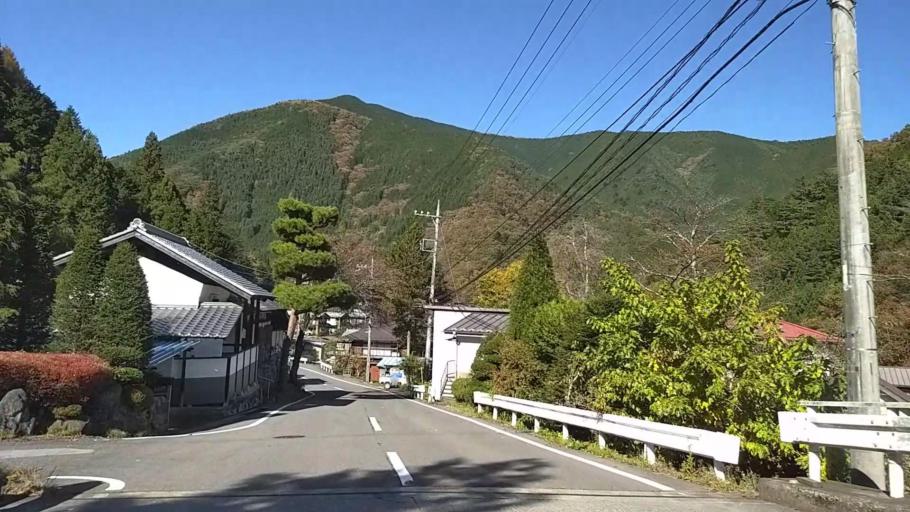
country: JP
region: Yamanashi
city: Otsuki
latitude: 35.7517
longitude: 138.9537
